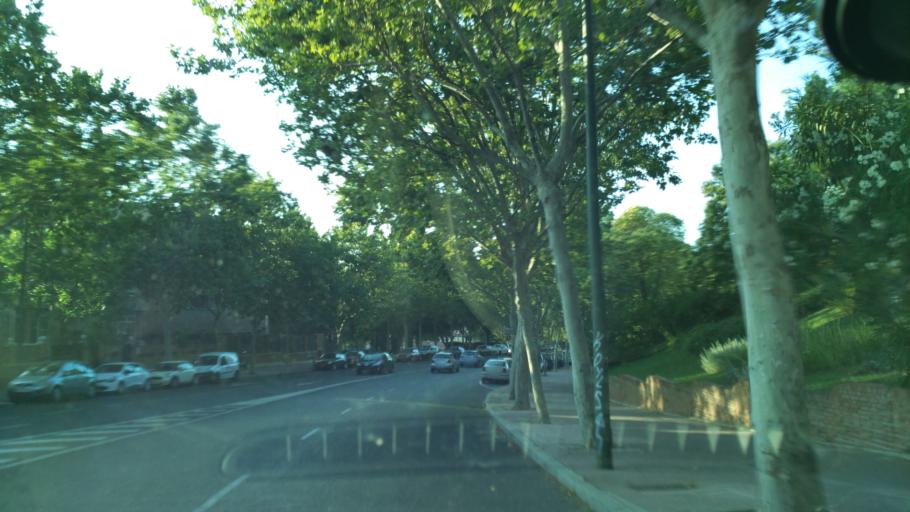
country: ES
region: Madrid
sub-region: Provincia de Madrid
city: Tetuan de las Victorias
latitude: 40.4630
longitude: -3.7199
